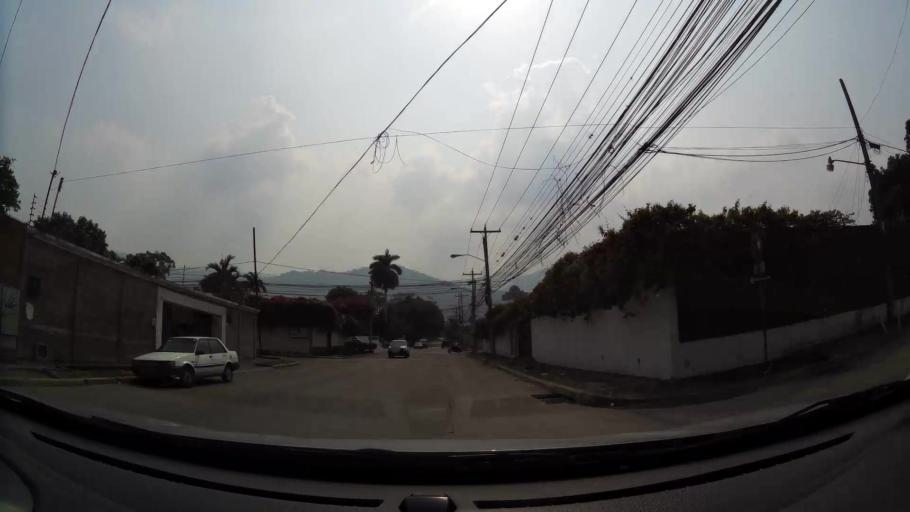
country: HN
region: Cortes
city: Armenta
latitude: 15.4985
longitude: -88.0398
